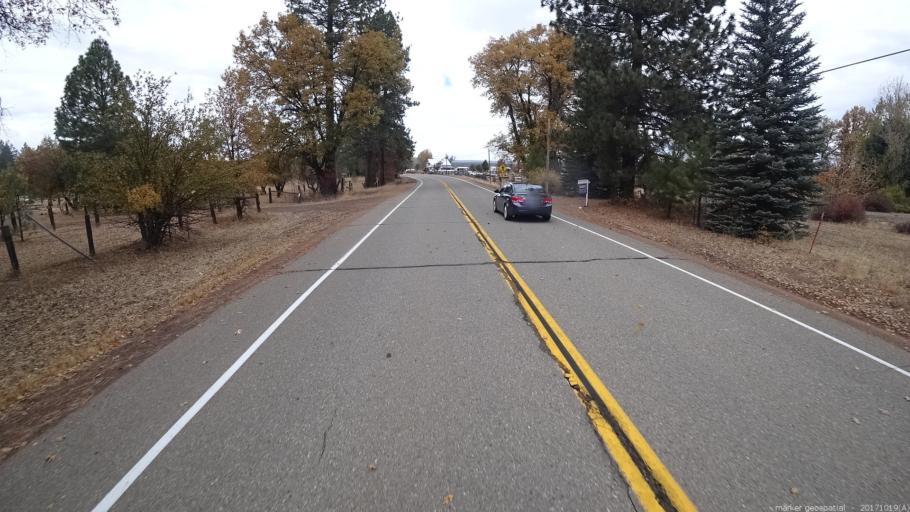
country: US
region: California
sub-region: Shasta County
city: Burney
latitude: 41.1106
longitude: -121.5634
